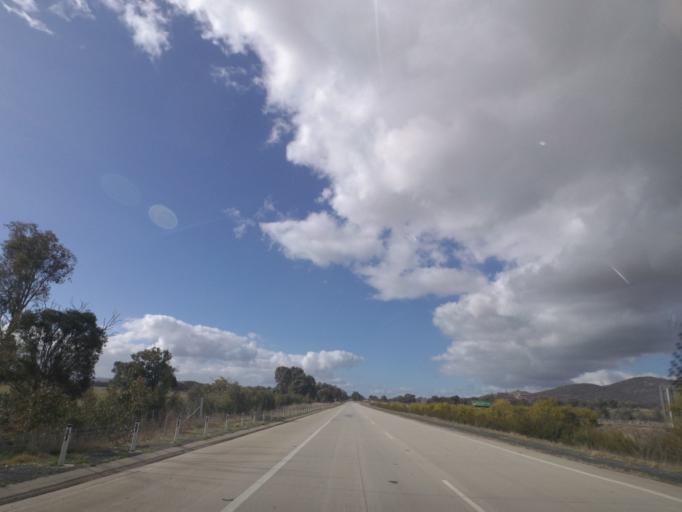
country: AU
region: New South Wales
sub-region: Greater Hume Shire
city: Holbrook
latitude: -35.6953
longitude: 147.3414
